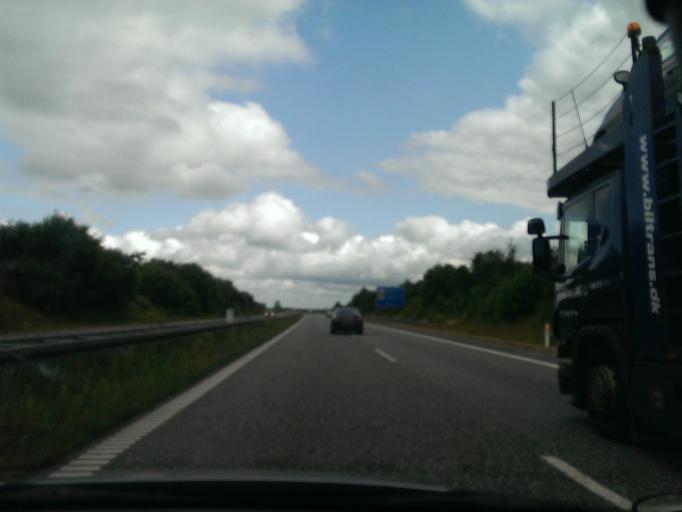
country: DK
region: North Denmark
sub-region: Mariagerfjord Kommune
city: Hobro
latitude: 56.6571
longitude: 9.7367
